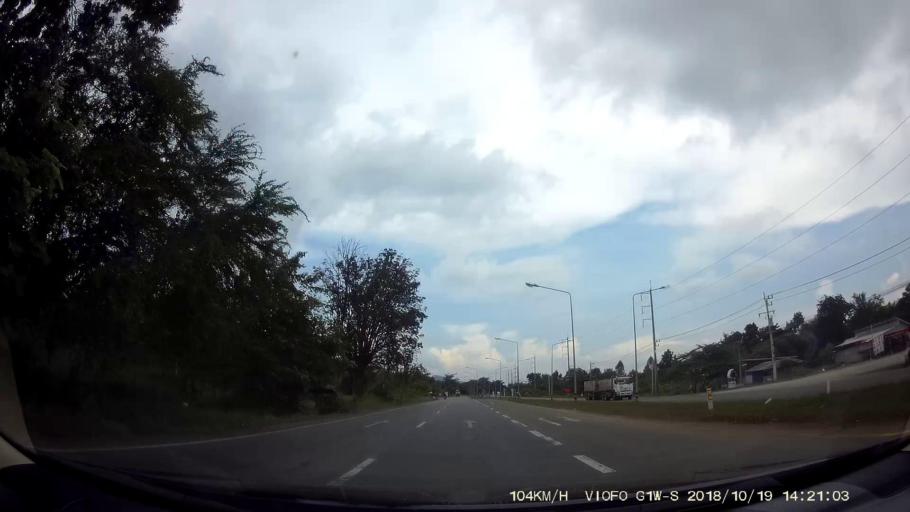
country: TH
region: Chaiyaphum
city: Kaeng Khro
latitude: 16.0479
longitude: 102.2621
